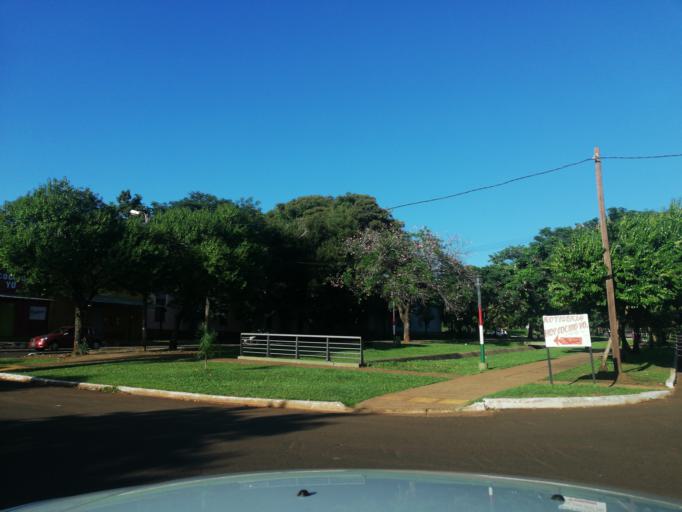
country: AR
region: Misiones
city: Garupa
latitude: -27.4797
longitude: -55.8284
